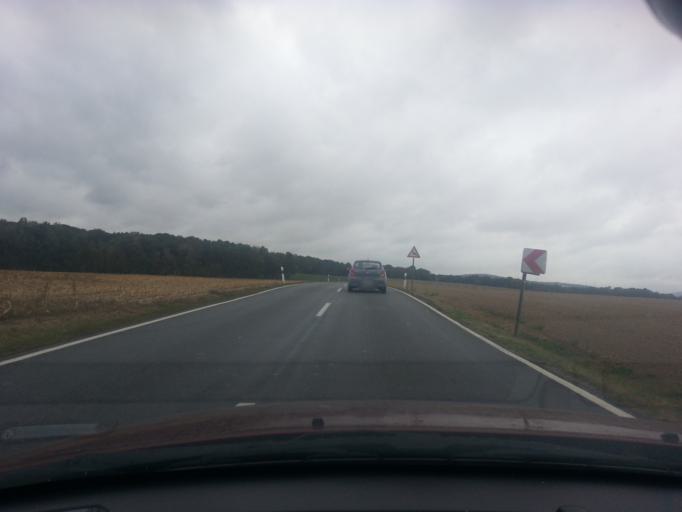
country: DE
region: Saxony
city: Markersdorf
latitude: 51.1112
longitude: 14.9160
